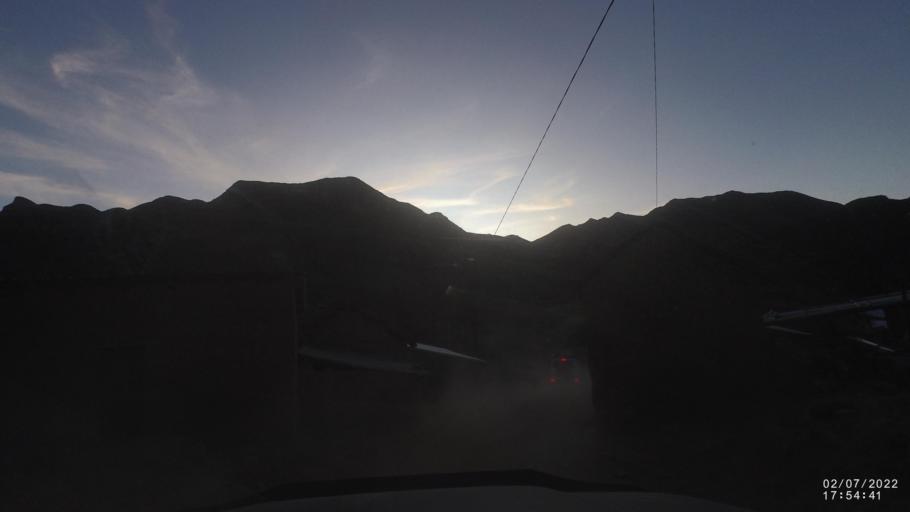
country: BO
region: Cochabamba
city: Irpa Irpa
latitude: -17.8439
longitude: -66.6176
